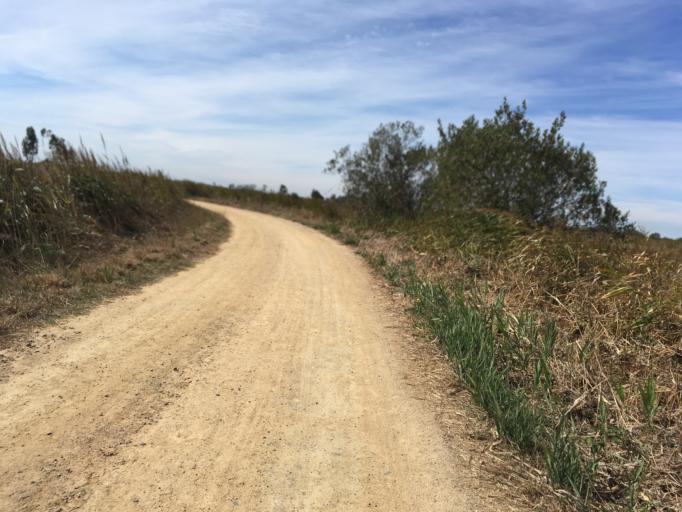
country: PT
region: Aveiro
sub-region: Estarreja
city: Salreu
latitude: 40.7317
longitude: -8.5725
